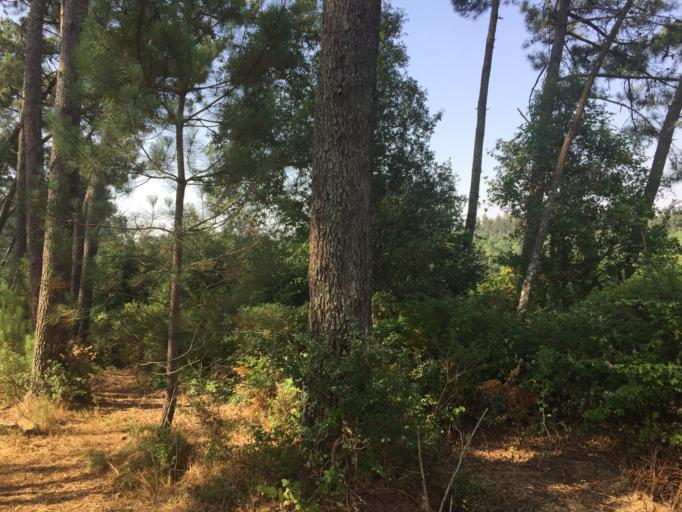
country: PT
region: Coimbra
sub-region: Cantanhede
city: Cantanhede
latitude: 40.4252
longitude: -8.5459
